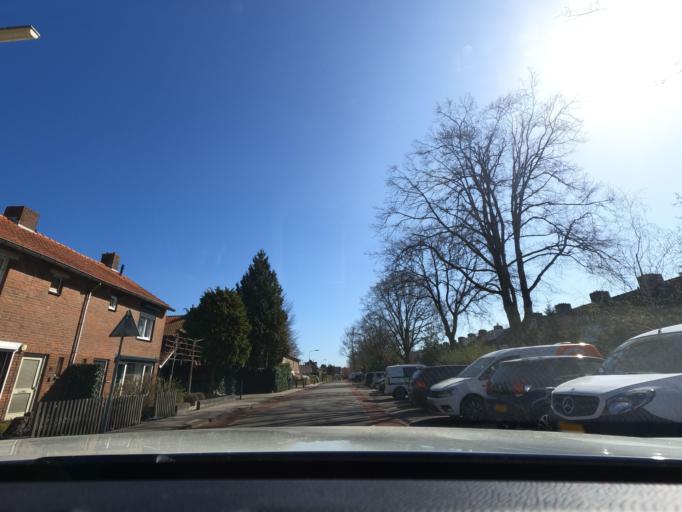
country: NL
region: Gelderland
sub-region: Gemeente Oldebroek
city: Oldebroek
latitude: 52.4158
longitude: 5.8762
